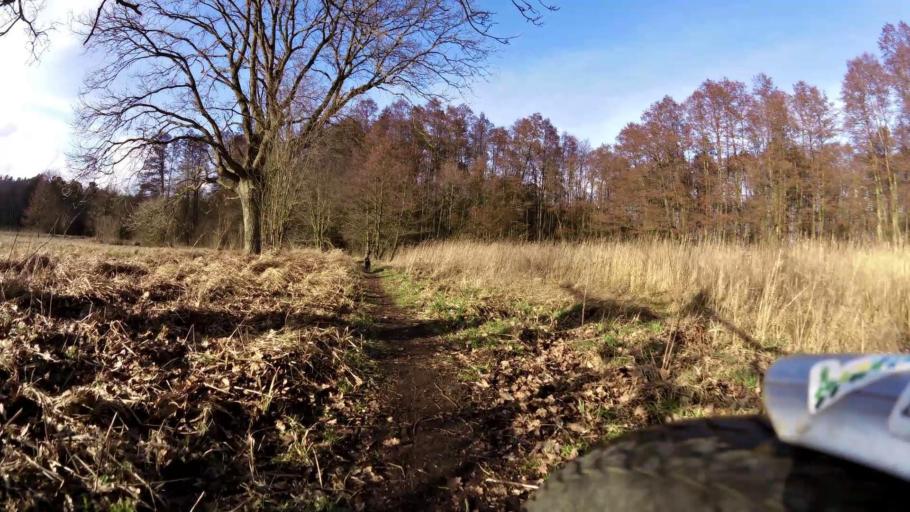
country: PL
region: West Pomeranian Voivodeship
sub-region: Powiat kamienski
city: Wolin
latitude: 53.8465
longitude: 14.7067
